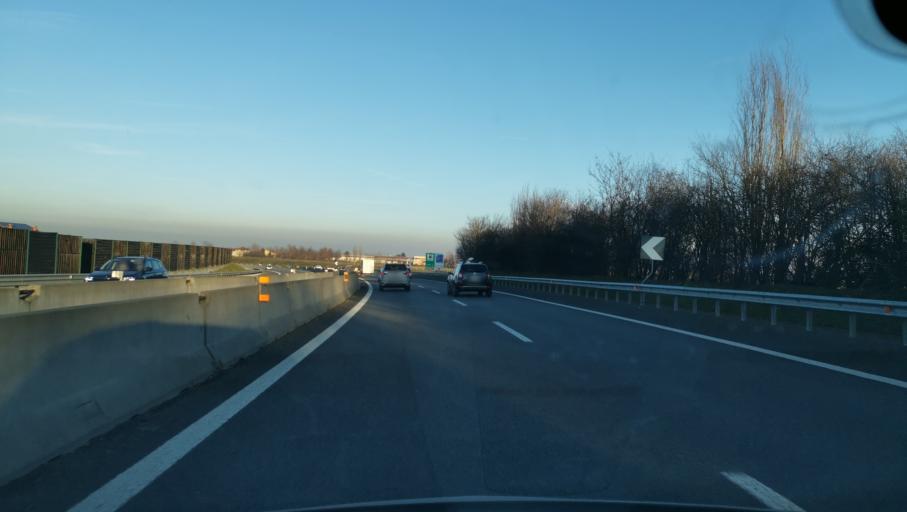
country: IT
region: Piedmont
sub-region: Provincia di Torino
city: Piscina
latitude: 44.9009
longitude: 7.4195
